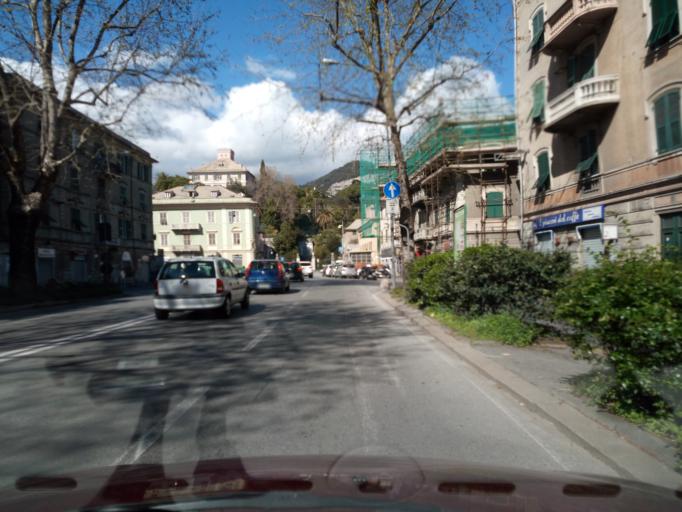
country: IT
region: Liguria
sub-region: Provincia di Genova
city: San Teodoro
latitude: 44.4252
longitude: 8.8441
